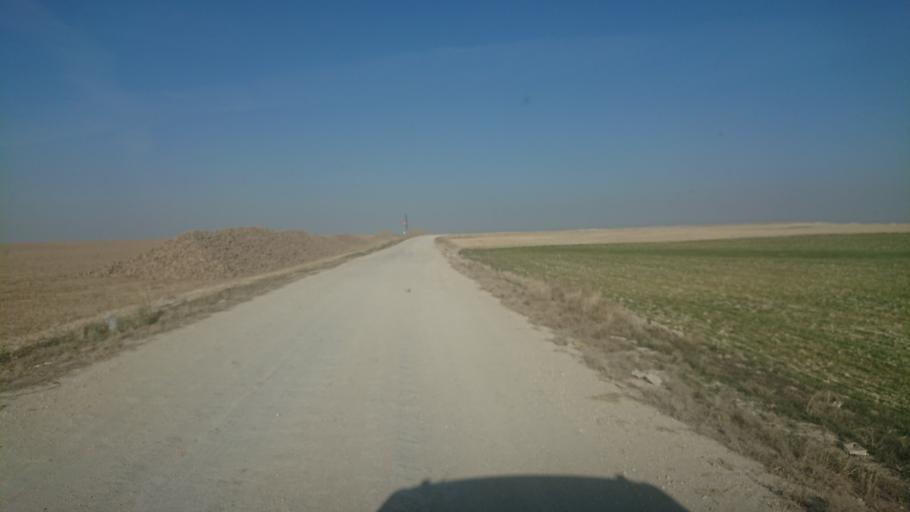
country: TR
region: Aksaray
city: Sultanhani
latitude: 38.0505
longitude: 33.6106
